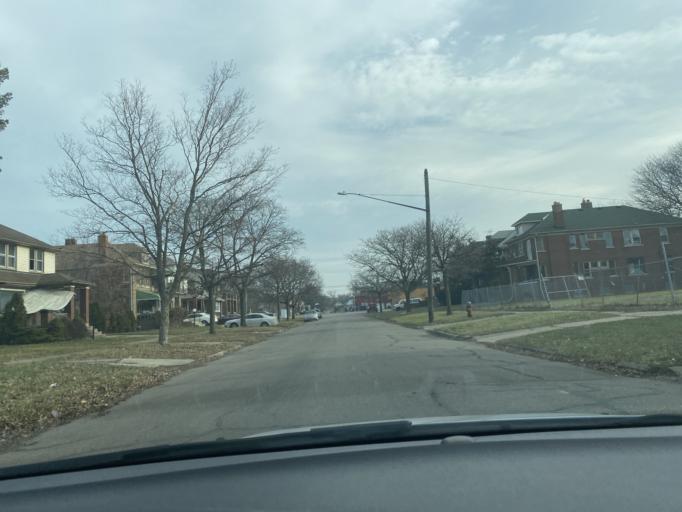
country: US
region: Michigan
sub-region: Wayne County
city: Highland Park
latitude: 42.3752
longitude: -83.1407
